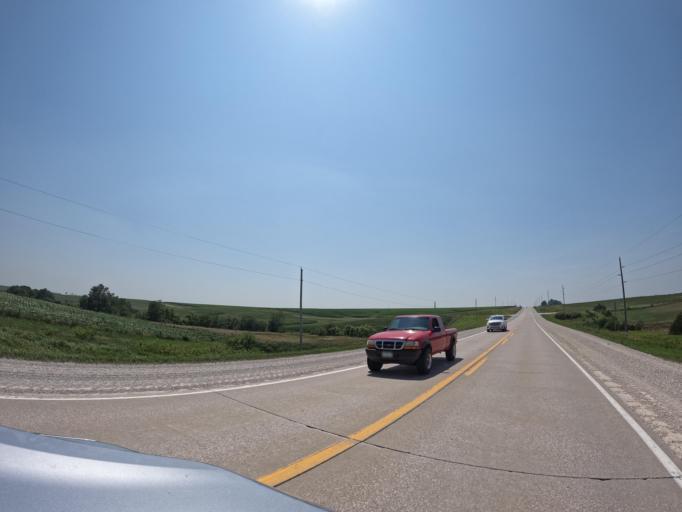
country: US
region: Iowa
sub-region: Keokuk County
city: Sigourney
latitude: 41.3368
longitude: -92.2554
